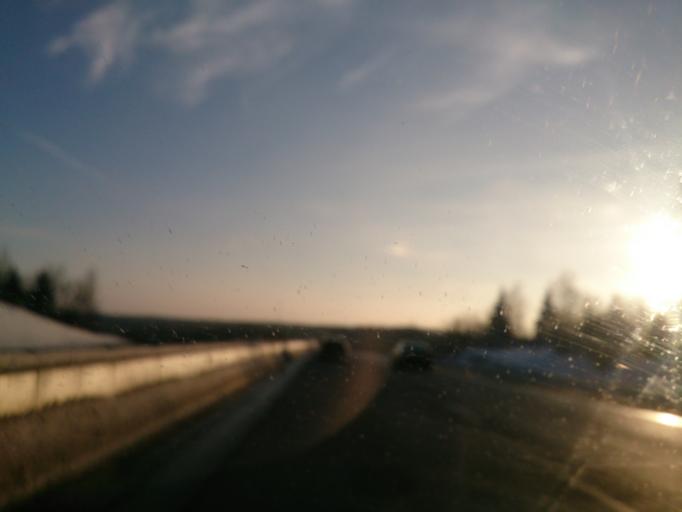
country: SE
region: OEstergoetland
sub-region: Norrkopings Kommun
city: Kimstad
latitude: 58.5130
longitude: 15.9939
